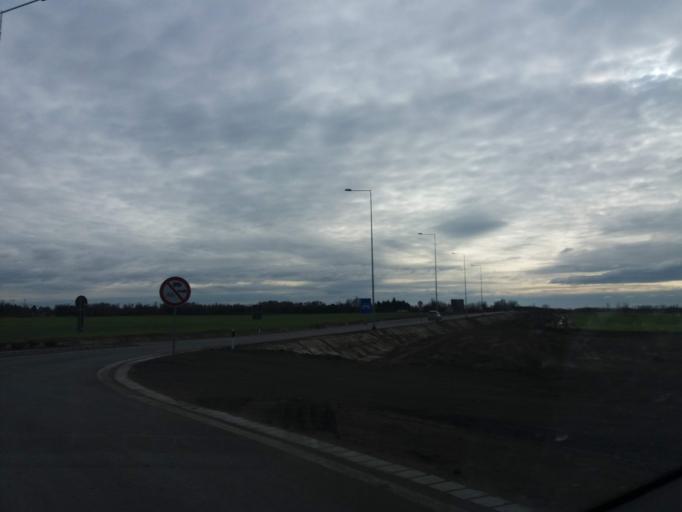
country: HU
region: Bacs-Kiskun
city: Tompa
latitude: 46.1634
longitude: 19.5629
